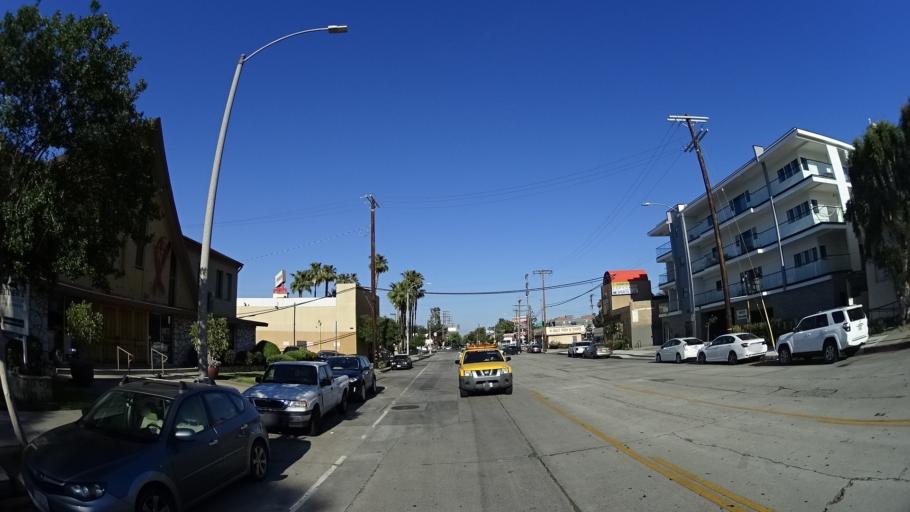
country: US
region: California
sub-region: Los Angeles County
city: North Hollywood
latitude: 34.1577
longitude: -118.3718
